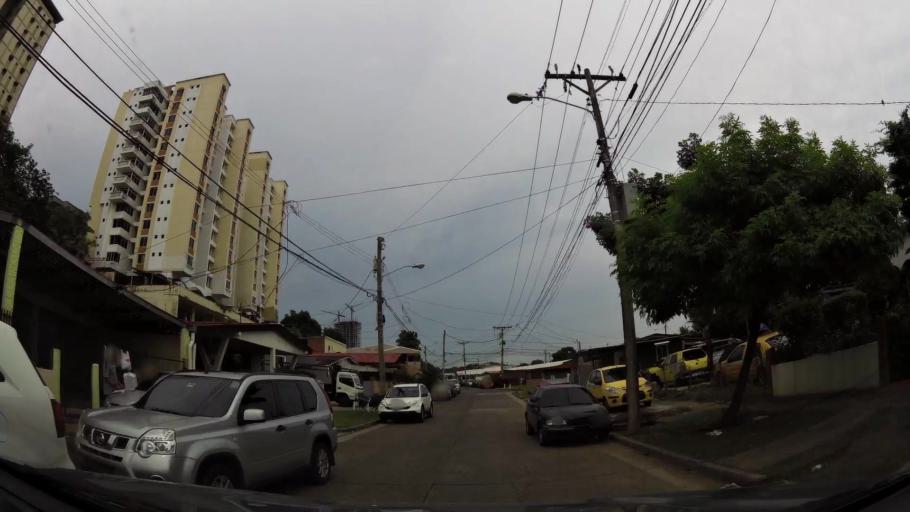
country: PA
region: Panama
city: Panama
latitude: 9.0226
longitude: -79.5238
